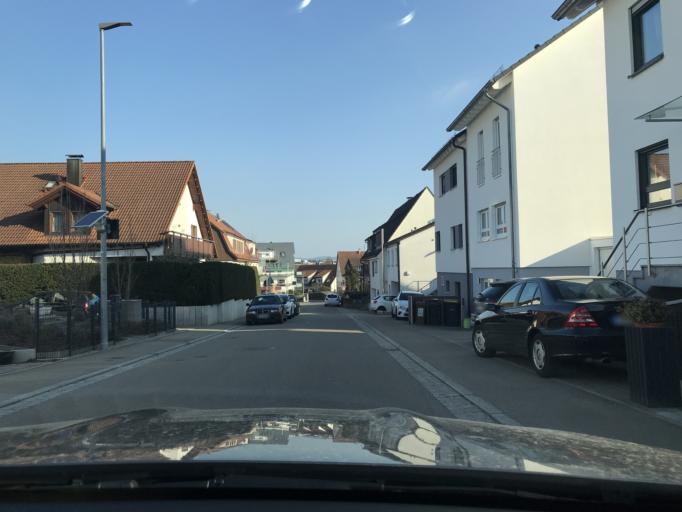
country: DE
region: Baden-Wuerttemberg
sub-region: Regierungsbezirk Stuttgart
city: Korb
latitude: 48.8299
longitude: 9.3713
